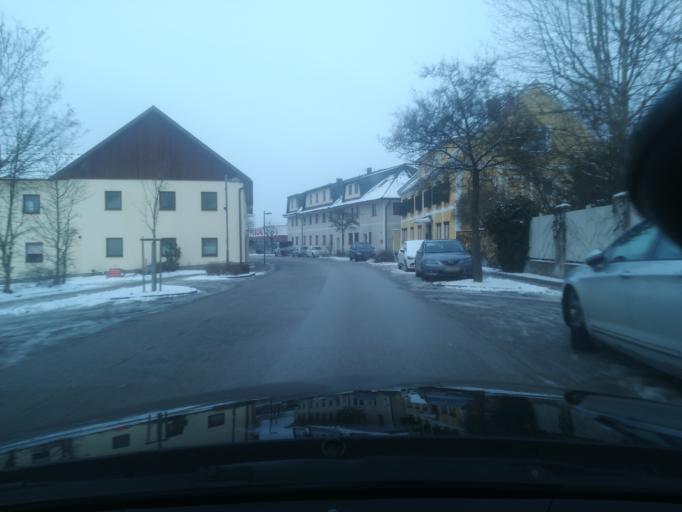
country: AT
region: Upper Austria
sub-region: Wels-Land
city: Marchtrenk
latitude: 48.1910
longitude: 14.1080
